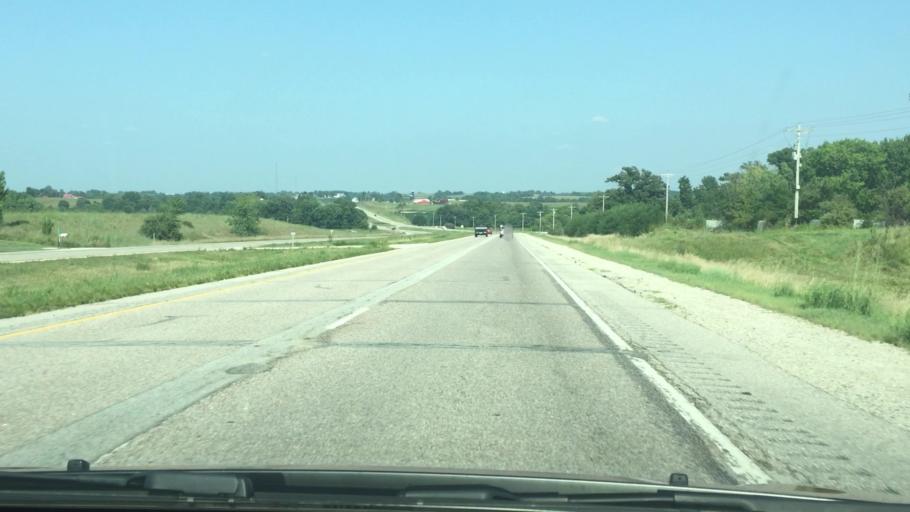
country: US
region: Iowa
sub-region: Cedar County
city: Durant
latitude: 41.5007
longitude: -90.9452
